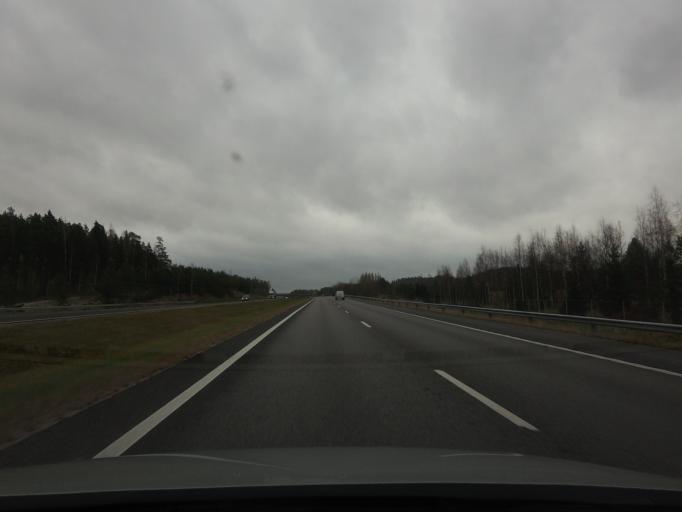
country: FI
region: Varsinais-Suomi
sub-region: Turku
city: Paimio
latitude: 60.4395
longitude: 22.6259
